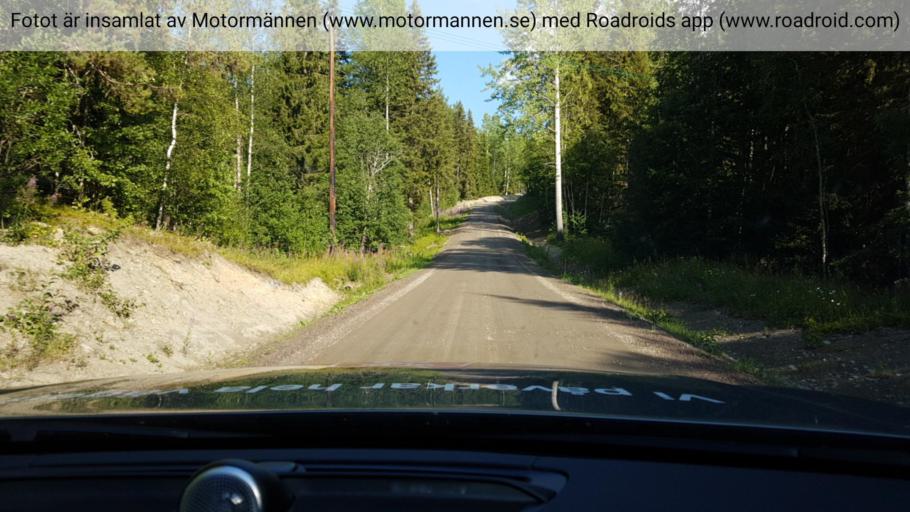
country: SE
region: Jaemtland
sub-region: Stroemsunds Kommun
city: Stroemsund
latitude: 63.9903
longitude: 16.0018
